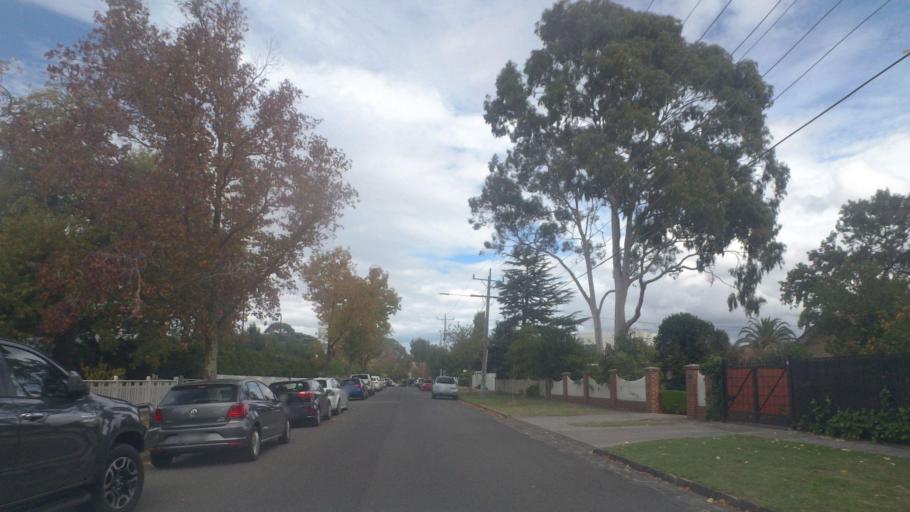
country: AU
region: Victoria
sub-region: Whitehorse
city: Surrey Hills
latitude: -37.8218
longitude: 145.1066
